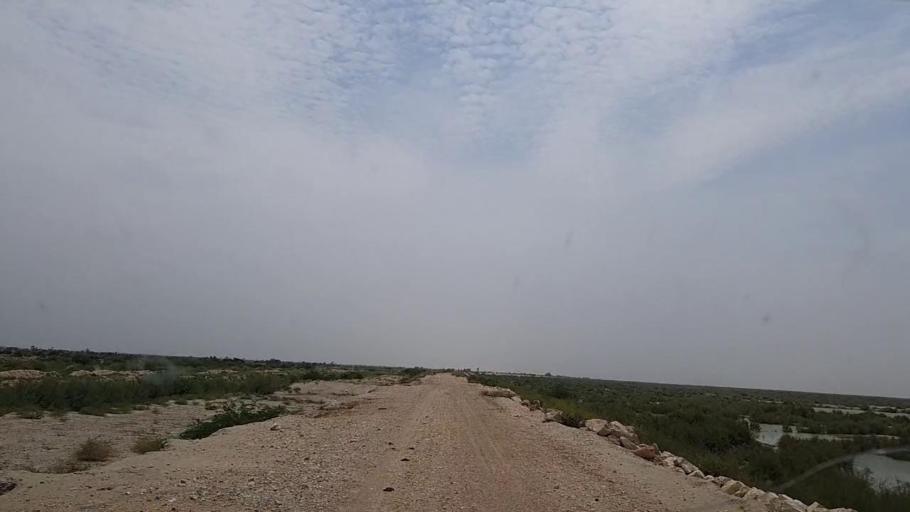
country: PK
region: Sindh
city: Phulji
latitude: 26.8700
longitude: 67.6476
